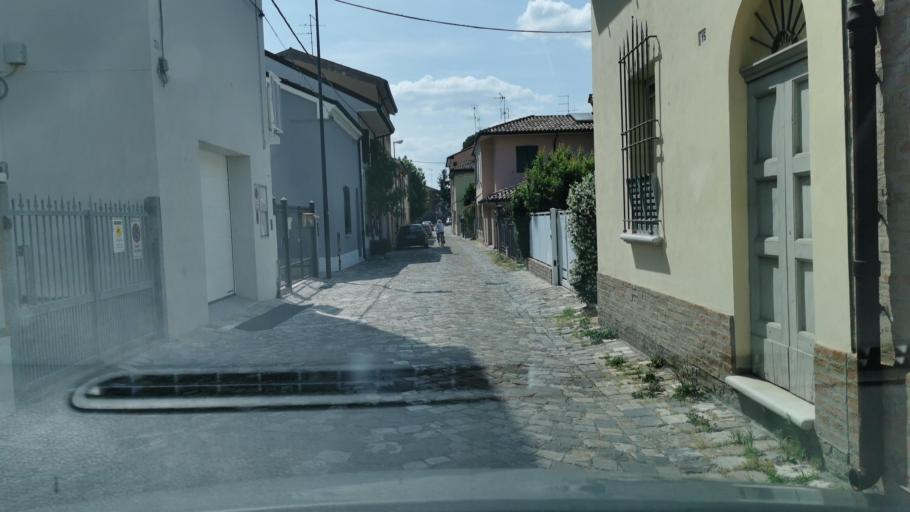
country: IT
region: Emilia-Romagna
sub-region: Provincia di Ravenna
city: Ravenna
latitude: 44.4096
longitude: 12.1996
